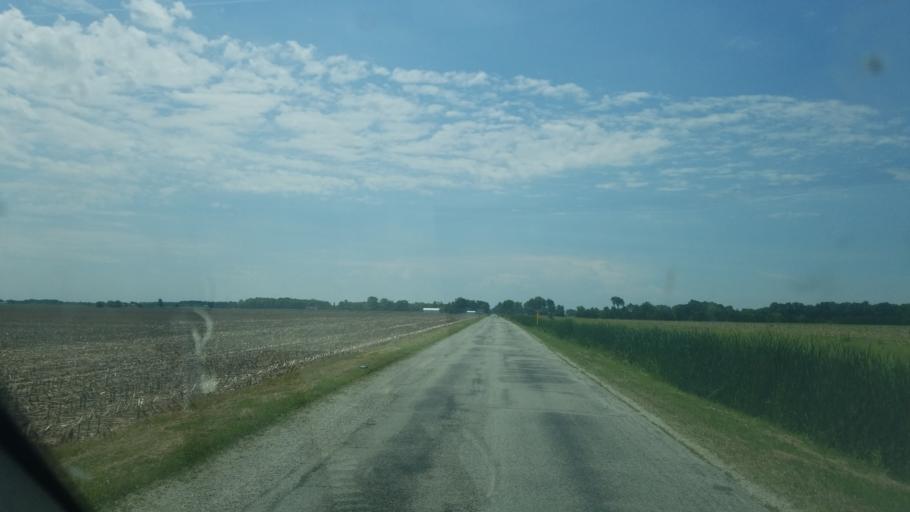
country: US
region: Ohio
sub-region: Wood County
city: North Baltimore
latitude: 41.2511
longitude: -83.6212
